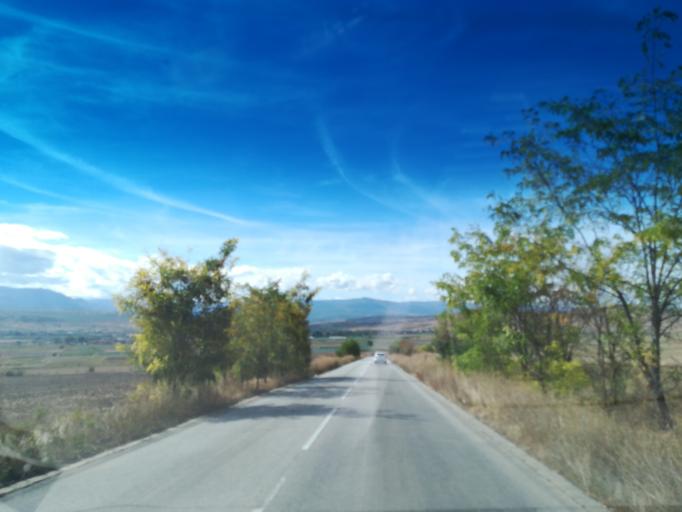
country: BG
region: Plovdiv
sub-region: Obshtina Krichim
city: Krichim
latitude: 42.0931
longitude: 24.4537
